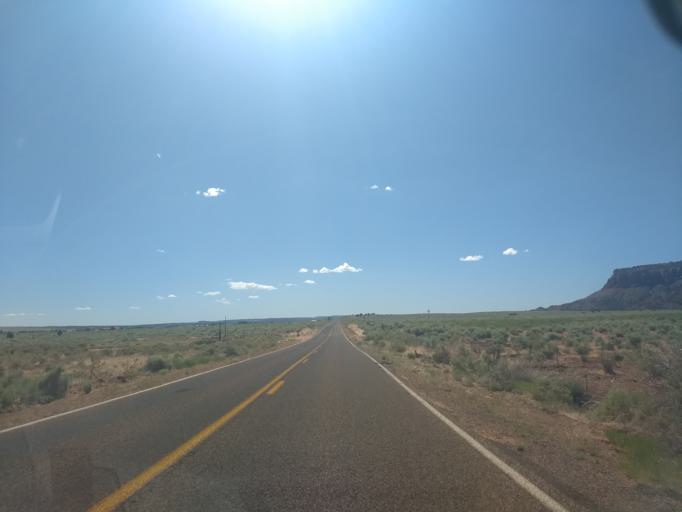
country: US
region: Arizona
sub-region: Mohave County
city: Colorado City
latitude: 36.9469
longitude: -112.9058
